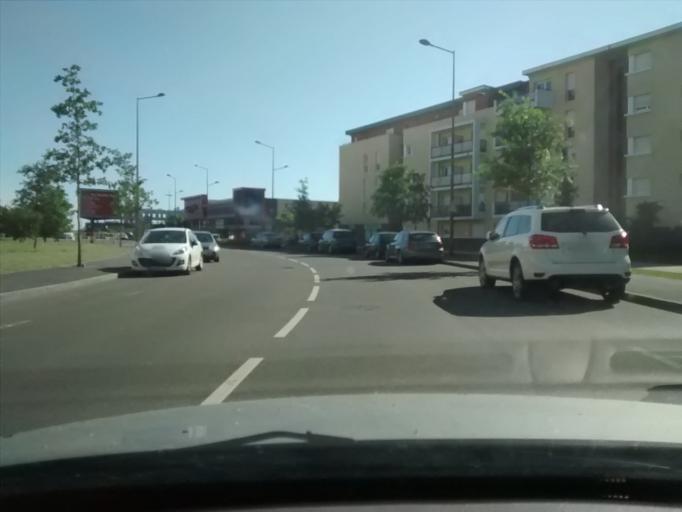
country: FR
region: Pays de la Loire
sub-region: Departement de la Sarthe
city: La Chapelle-Saint-Aubin
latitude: 48.0185
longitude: 0.1535
